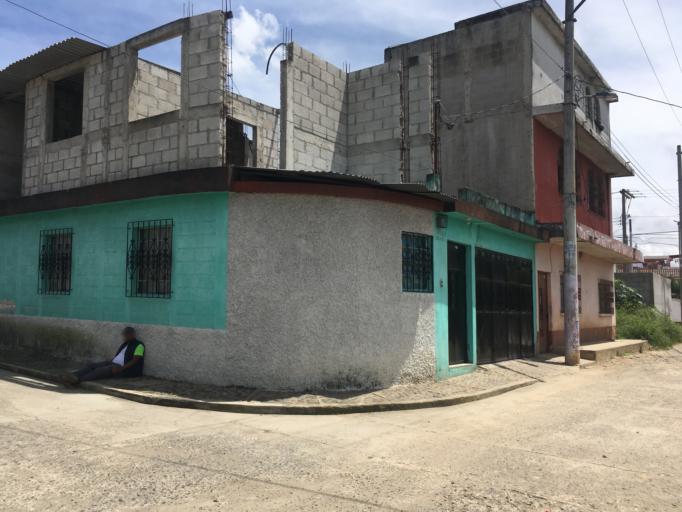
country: GT
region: Guatemala
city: Petapa
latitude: 14.5008
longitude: -90.5698
